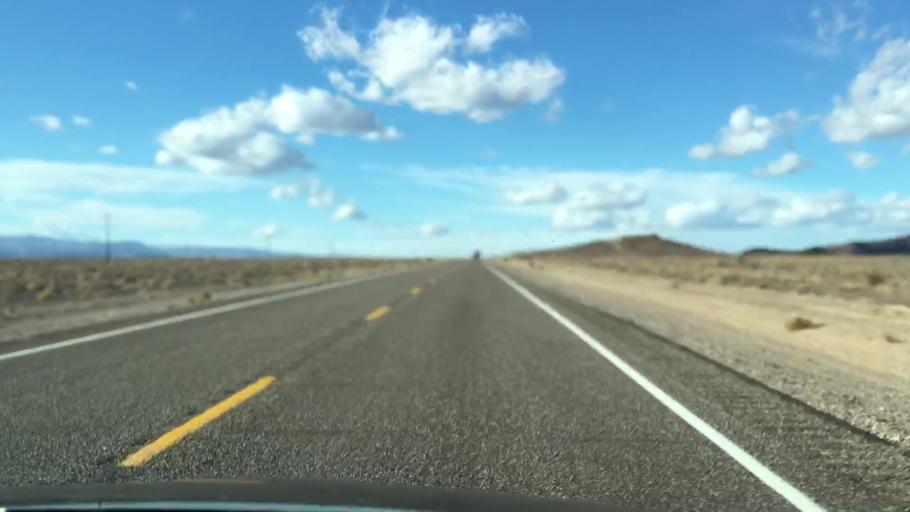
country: US
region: Nevada
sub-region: Nye County
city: Beatty
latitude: 37.1900
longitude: -116.9429
